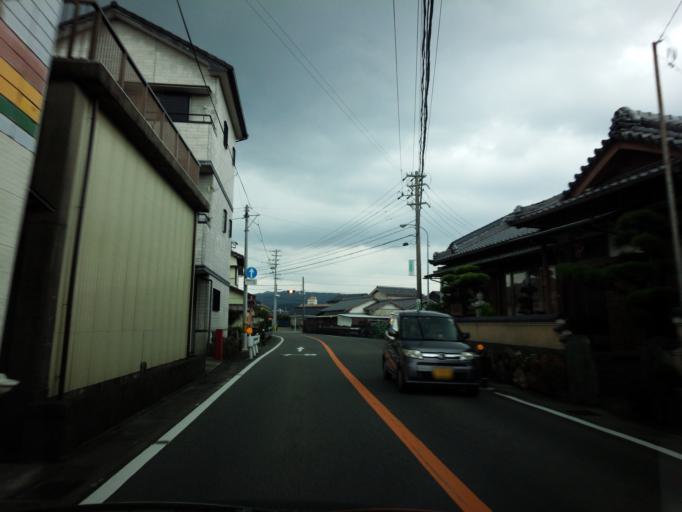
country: JP
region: Mie
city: Toba
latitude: 34.3657
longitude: 136.8091
